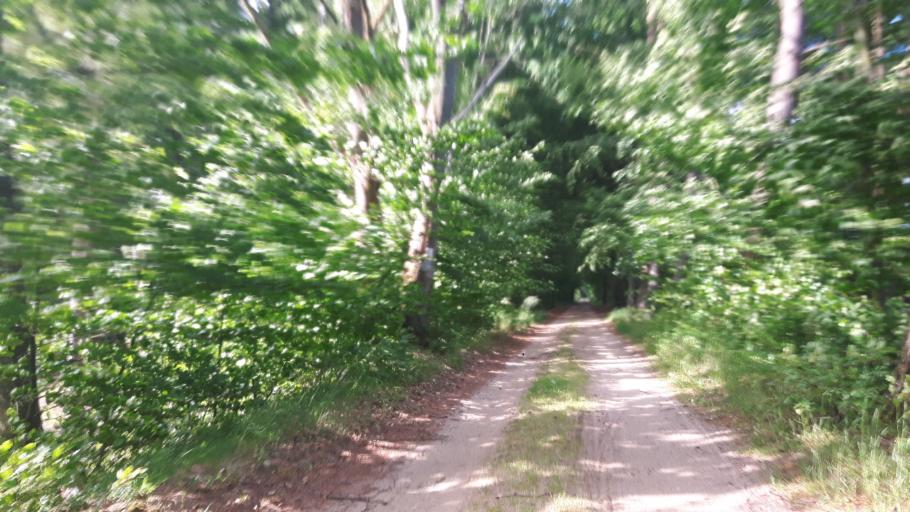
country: PL
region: Pomeranian Voivodeship
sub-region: Slupsk
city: Slupsk
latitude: 54.6055
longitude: 17.0212
